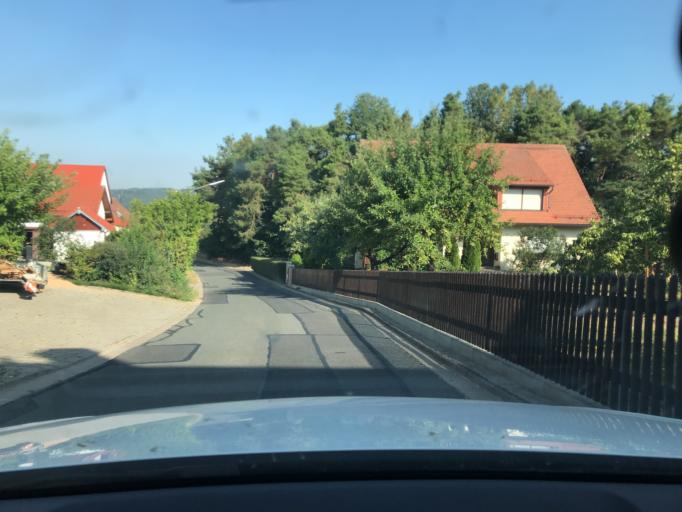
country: DE
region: Bavaria
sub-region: Upper Franconia
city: Pegnitz
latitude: 49.7692
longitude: 11.5998
